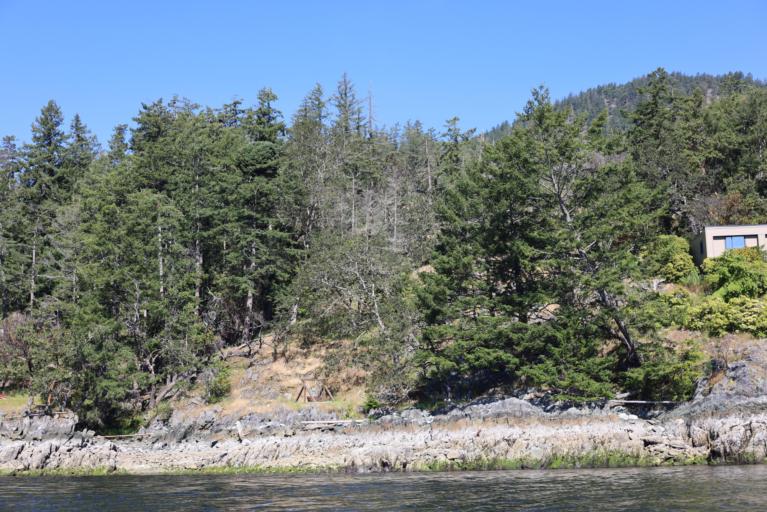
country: CA
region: British Columbia
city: North Cowichan
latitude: 48.8235
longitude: -123.5842
